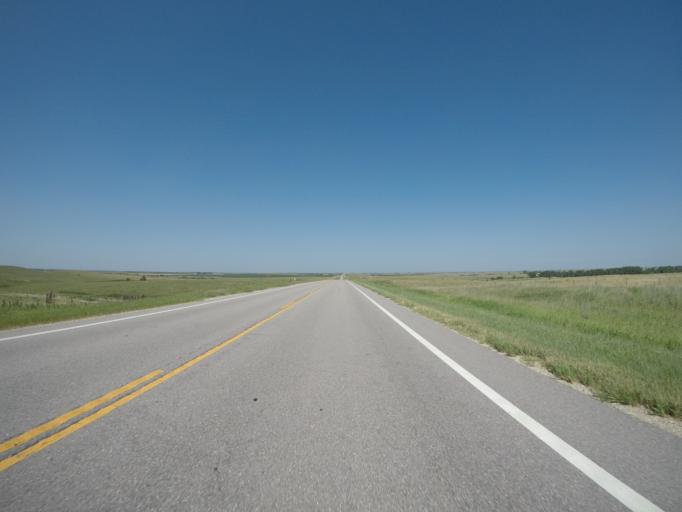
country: US
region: Kansas
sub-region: Cloud County
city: Concordia
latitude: 39.3647
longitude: -97.5117
